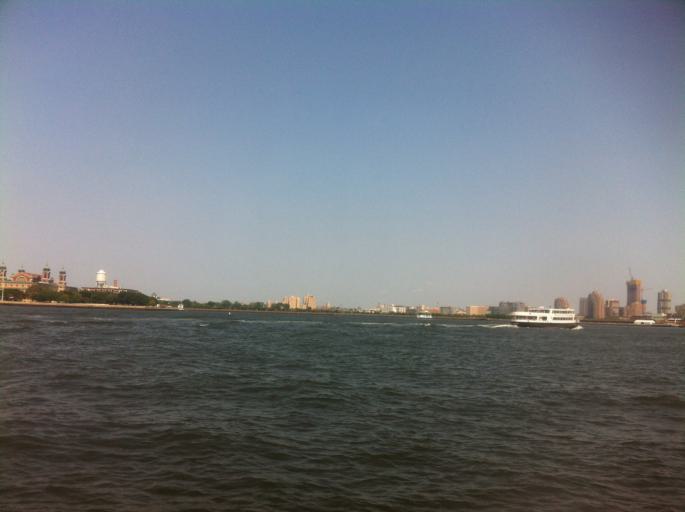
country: US
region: New York
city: New York City
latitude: 40.6965
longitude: -74.0320
